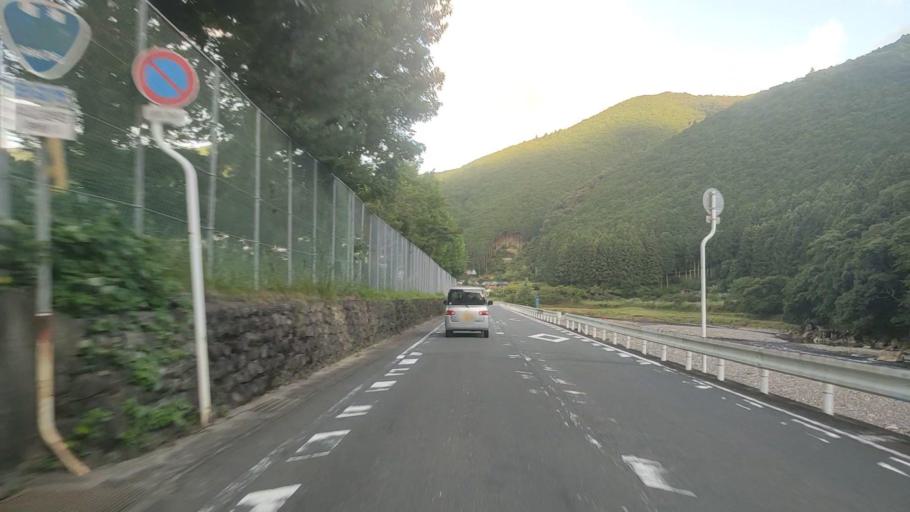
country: JP
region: Wakayama
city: Tanabe
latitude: 33.7880
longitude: 135.5084
